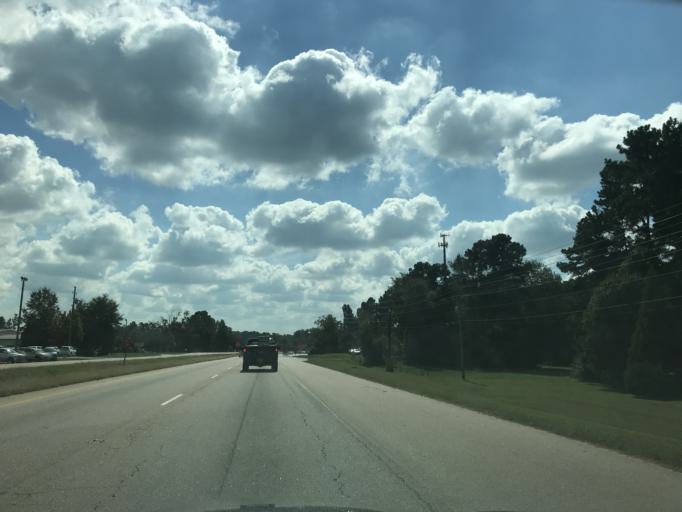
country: US
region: North Carolina
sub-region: Wake County
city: Wake Forest
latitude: 35.8973
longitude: -78.5586
